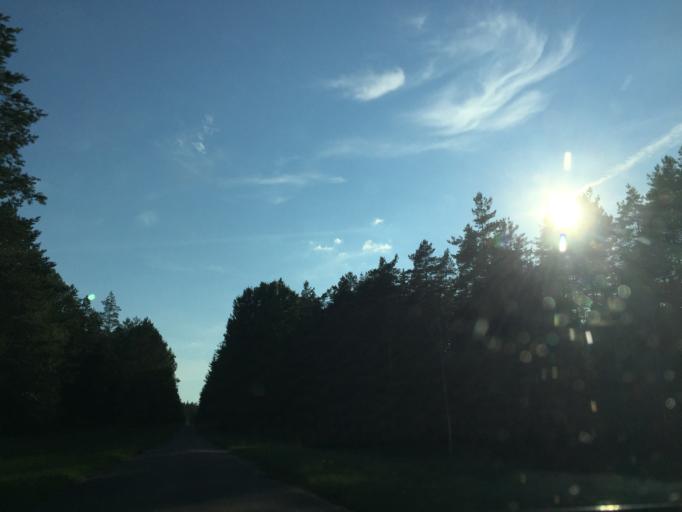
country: LV
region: Krimulda
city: Ragana
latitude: 57.1354
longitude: 24.7660
